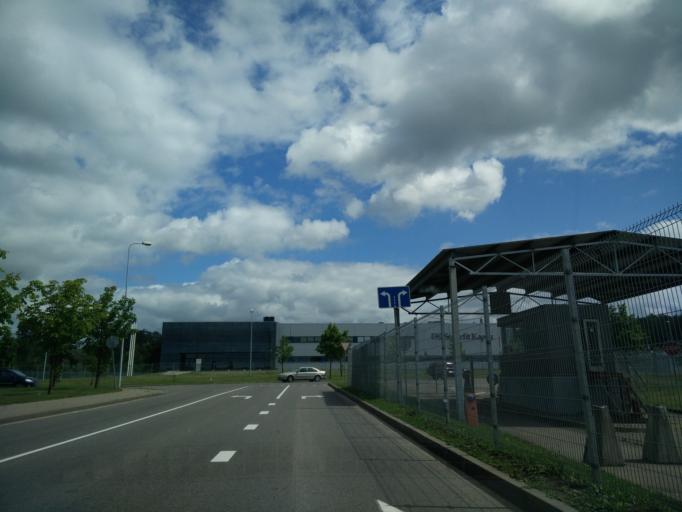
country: LT
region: Vilnius County
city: Pilaite
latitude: 54.6569
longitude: 25.1410
